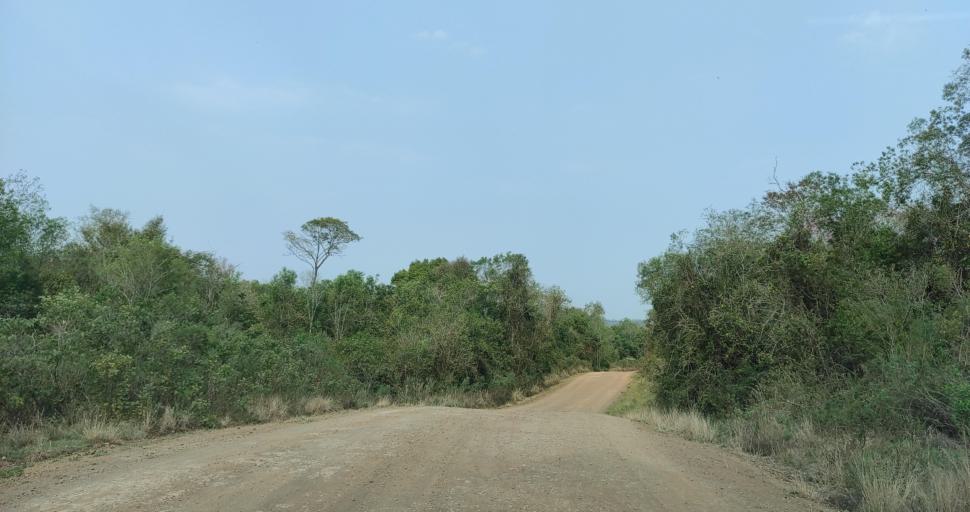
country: AR
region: Misiones
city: Cerro Cora
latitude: -27.5392
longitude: -55.5857
